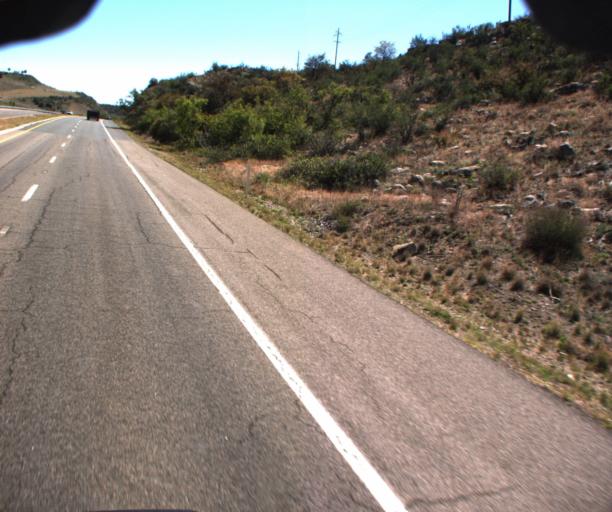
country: US
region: Arizona
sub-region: Yavapai County
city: Prescott
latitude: 34.5635
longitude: -112.4445
